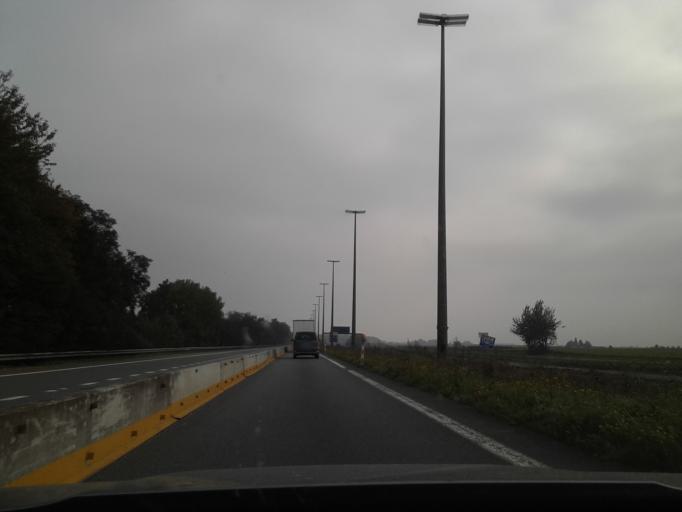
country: FR
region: Nord-Pas-de-Calais
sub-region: Departement du Nord
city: Camphin-en-Pevele
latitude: 50.6052
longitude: 3.2800
